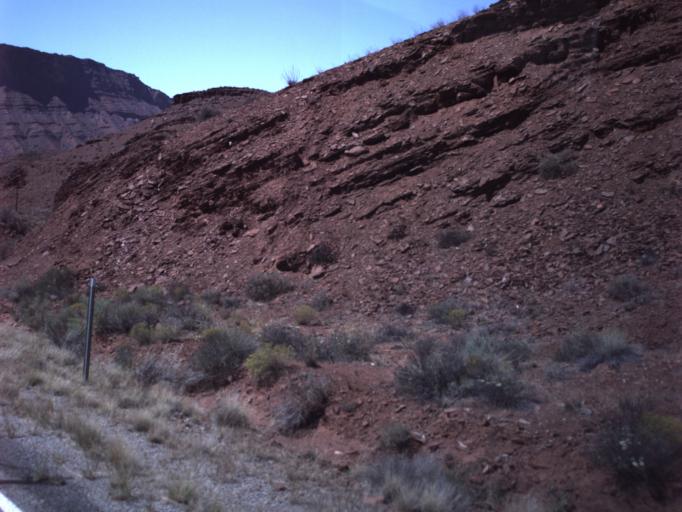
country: US
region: Utah
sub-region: Grand County
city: Moab
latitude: 38.7050
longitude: -109.3849
